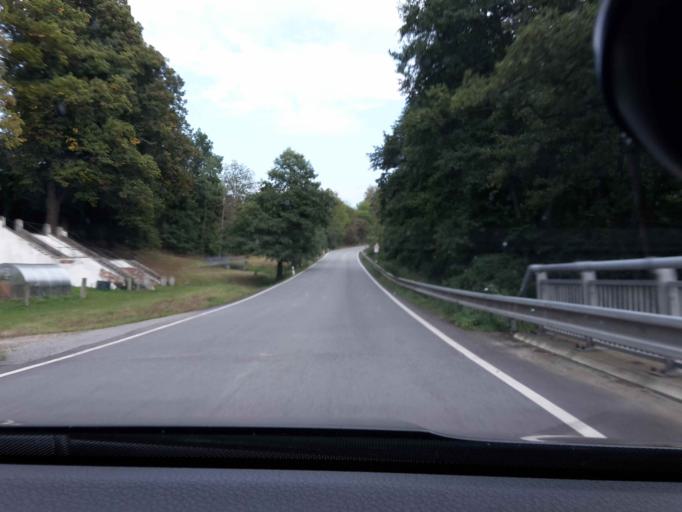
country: CZ
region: Vysocina
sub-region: Okres Jihlava
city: Telc
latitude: 49.1457
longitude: 15.5444
